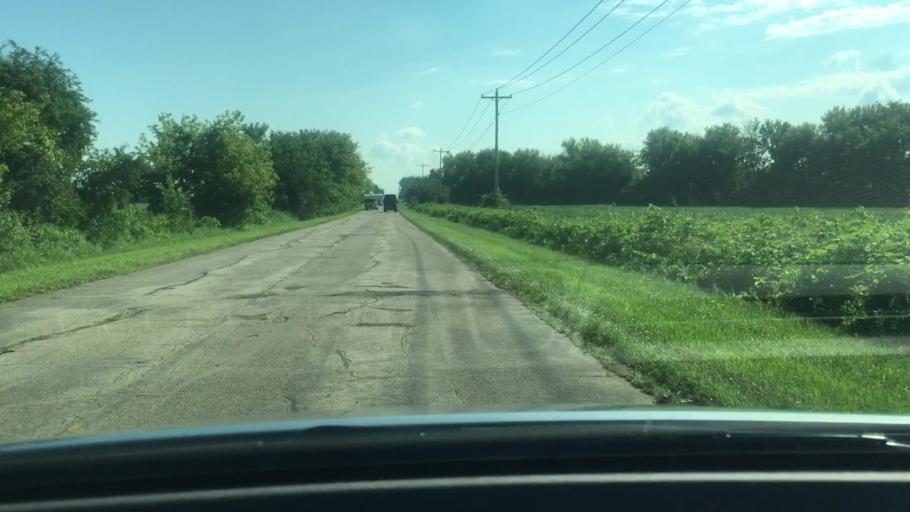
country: US
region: Wisconsin
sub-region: Winnebago County
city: Oshkosh
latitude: 43.9626
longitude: -88.5717
